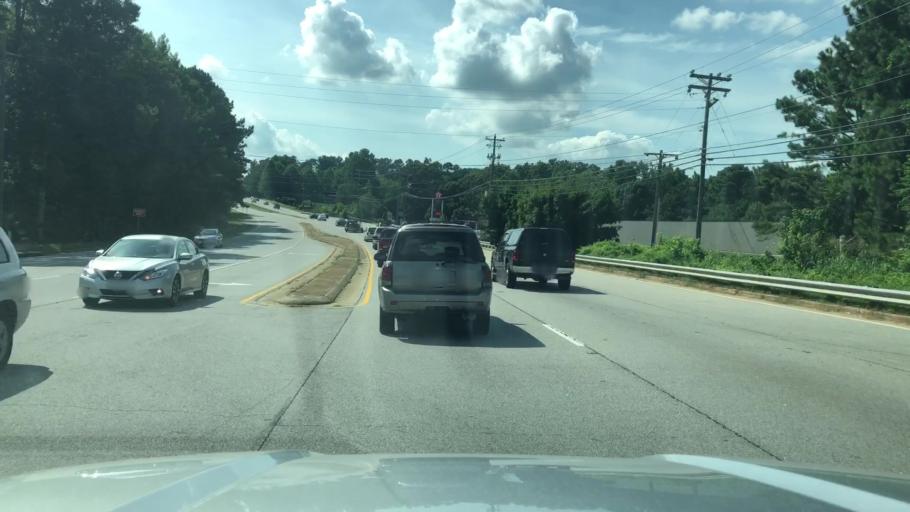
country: US
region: Georgia
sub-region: Douglas County
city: Lithia Springs
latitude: 33.7391
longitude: -84.6757
